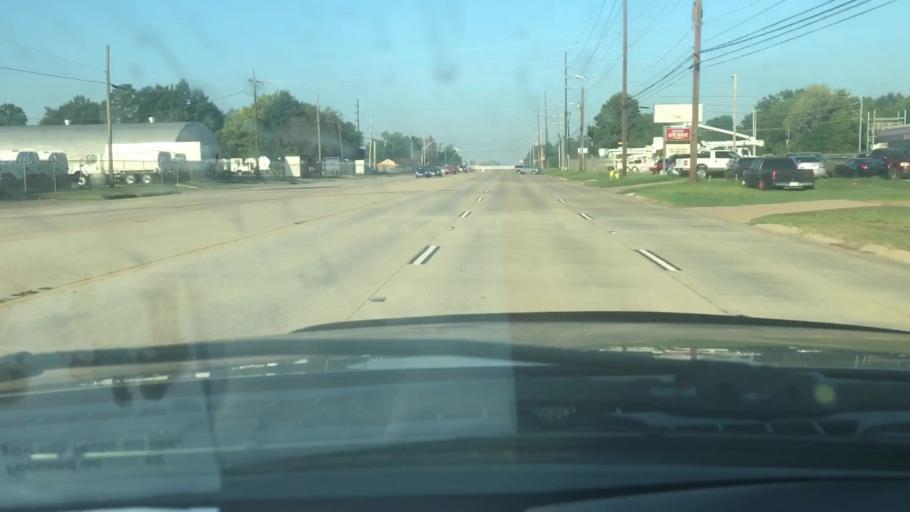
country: US
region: Texas
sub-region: Bowie County
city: Wake Village
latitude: 33.4198
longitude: -94.0886
